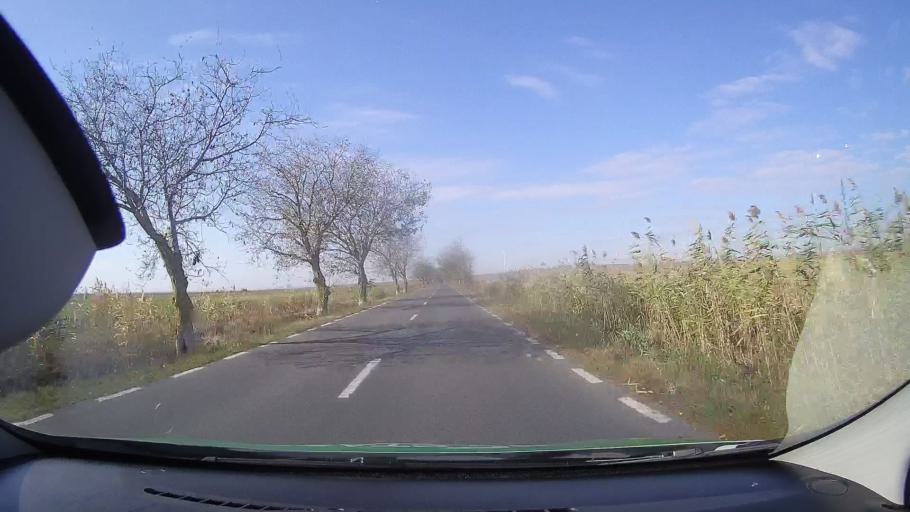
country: RO
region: Tulcea
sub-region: Comuna Bestepe
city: Bestepe
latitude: 45.0278
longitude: 29.0178
